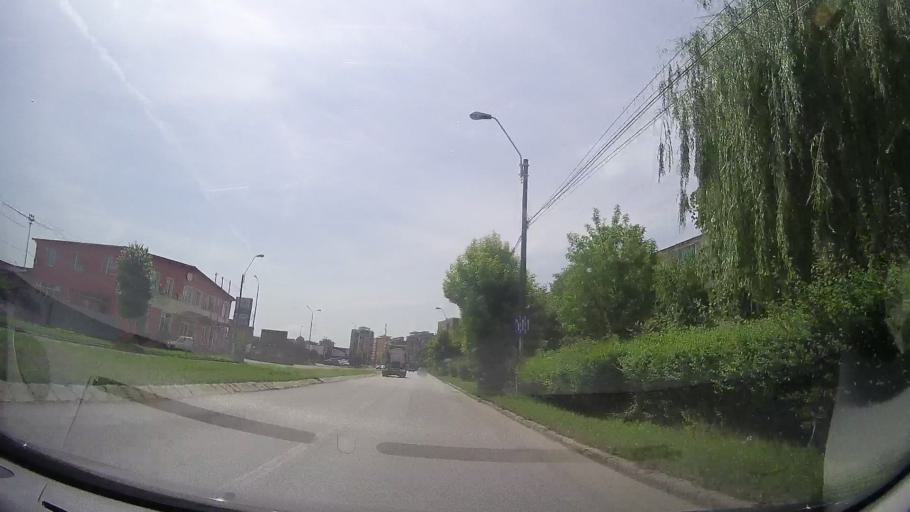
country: RO
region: Hunedoara
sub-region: Municipiul Deva
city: Deva
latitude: 45.8864
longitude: 22.9076
